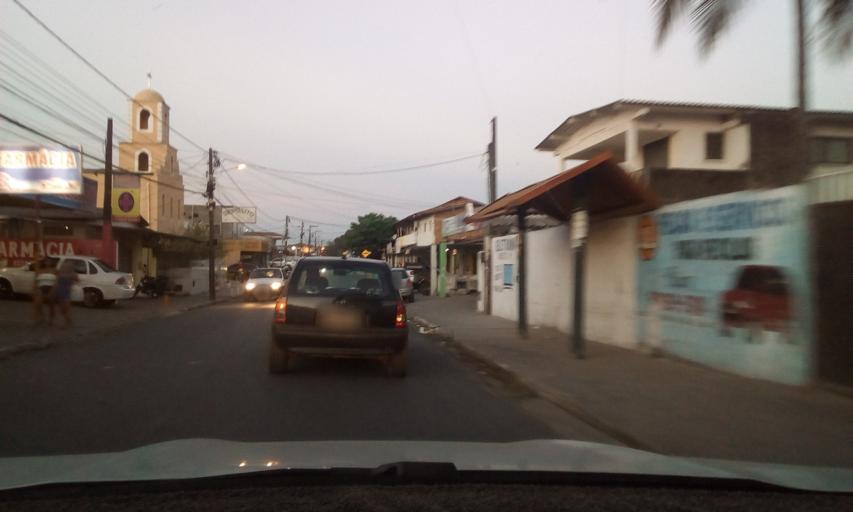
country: BR
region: Paraiba
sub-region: Bayeux
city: Bayeux
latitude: -7.1706
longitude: -34.9127
